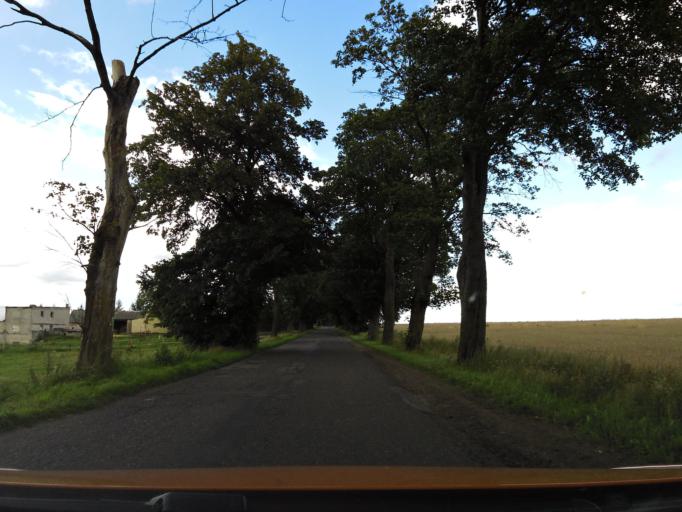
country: PL
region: West Pomeranian Voivodeship
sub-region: Powiat kolobrzeski
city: Ryman
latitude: 54.0040
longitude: 15.5026
